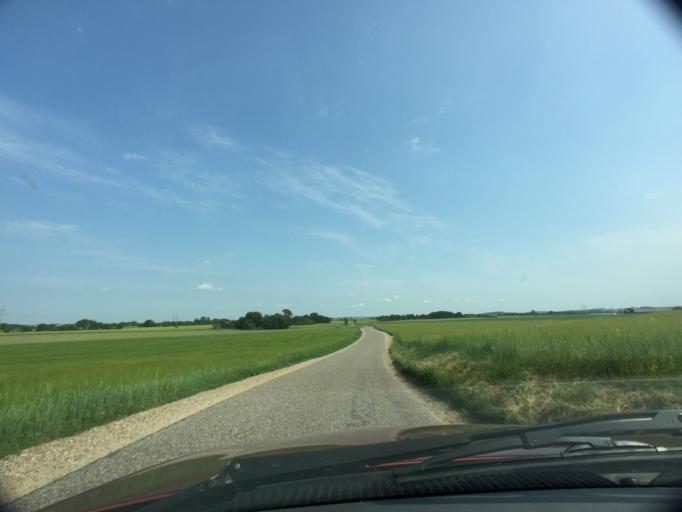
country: DK
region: Central Jutland
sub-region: Favrskov Kommune
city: Hammel
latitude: 56.2472
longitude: 9.7420
